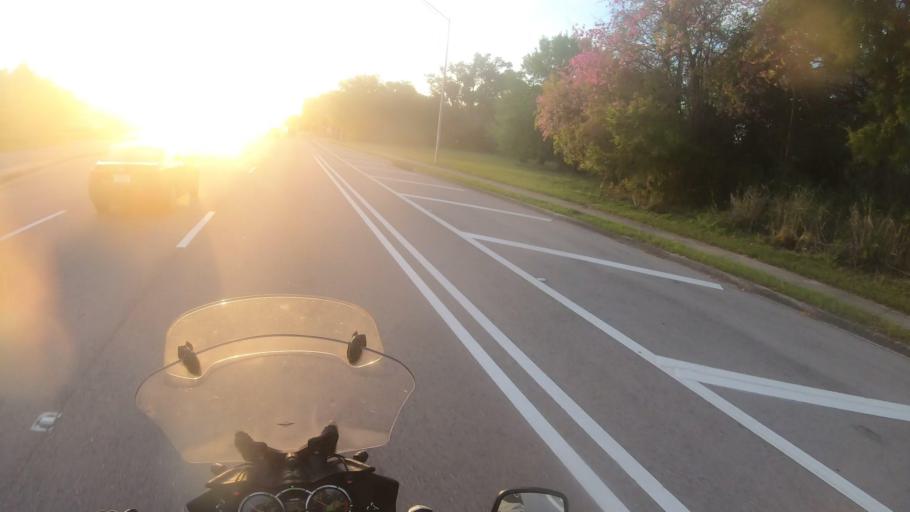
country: US
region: Florida
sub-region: Manatee County
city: Samoset
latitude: 27.4483
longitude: -82.5324
